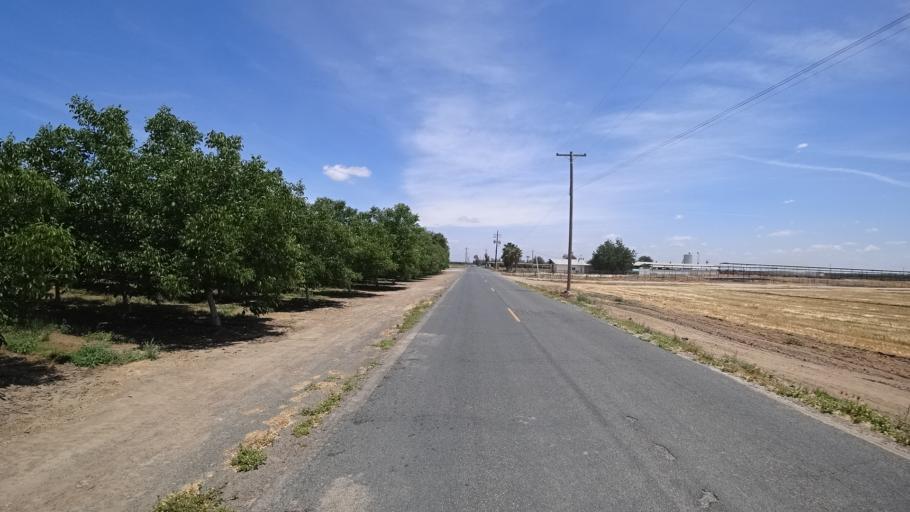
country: US
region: California
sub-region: Kings County
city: Armona
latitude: 36.2838
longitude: -119.6859
